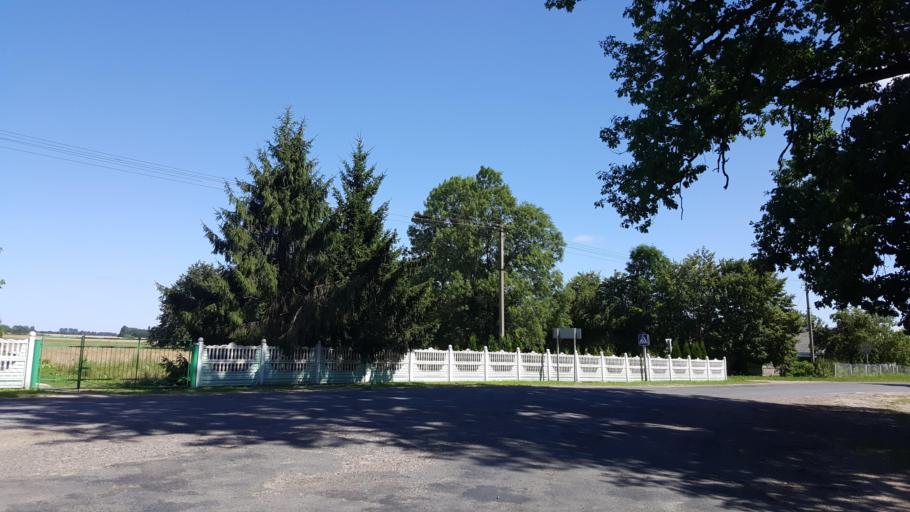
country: BY
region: Brest
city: Horad Kobryn
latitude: 52.3005
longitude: 24.3681
